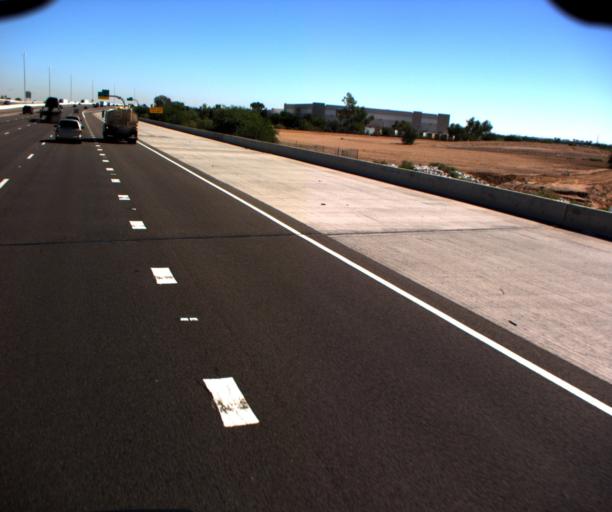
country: US
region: Arizona
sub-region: Maricopa County
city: Goodyear
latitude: 33.4611
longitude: -112.3843
